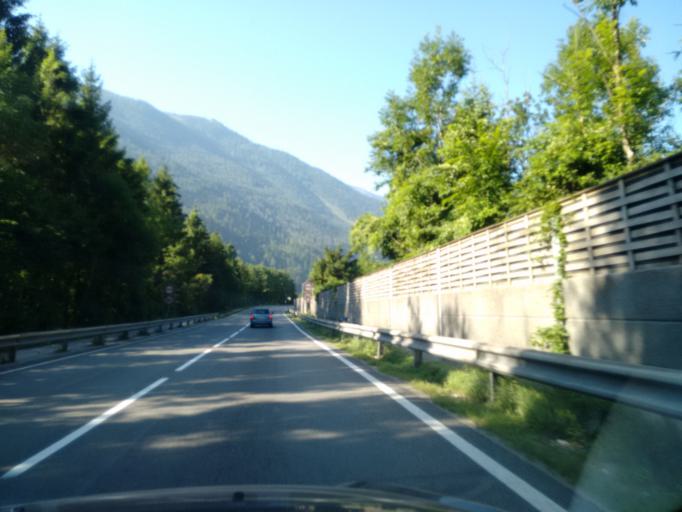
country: AT
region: Upper Austria
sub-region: Politischer Bezirk Gmunden
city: Ebensee
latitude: 47.7779
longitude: 13.7293
